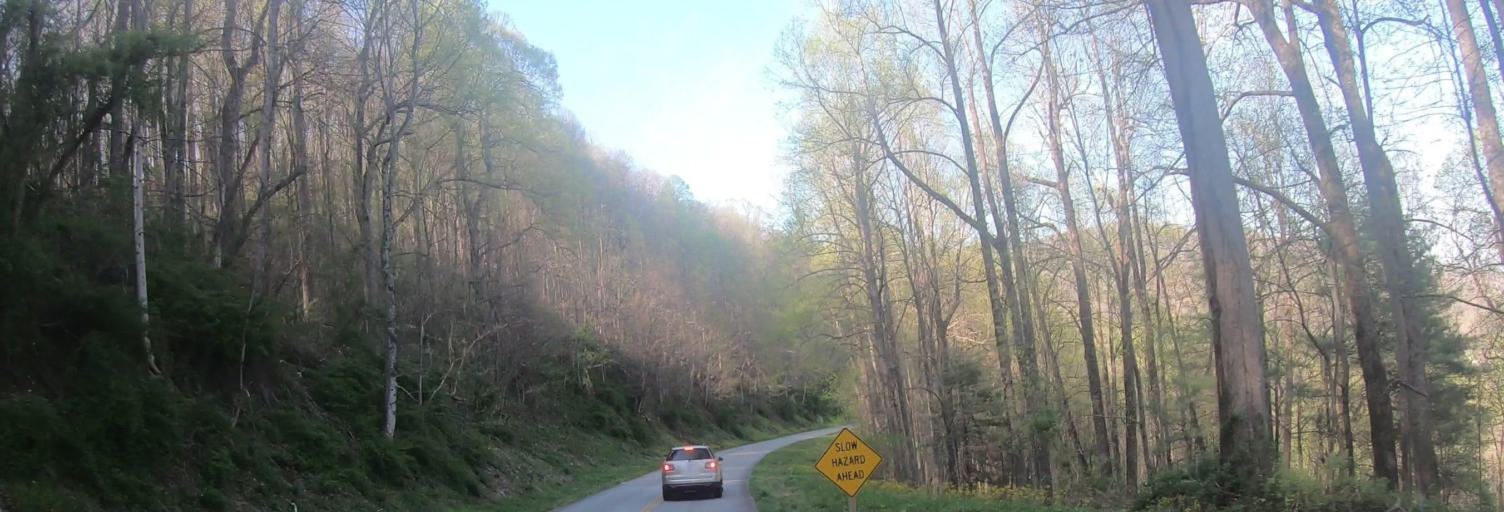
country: US
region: North Carolina
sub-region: Watauga County
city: Boone
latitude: 36.2239
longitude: -81.5038
